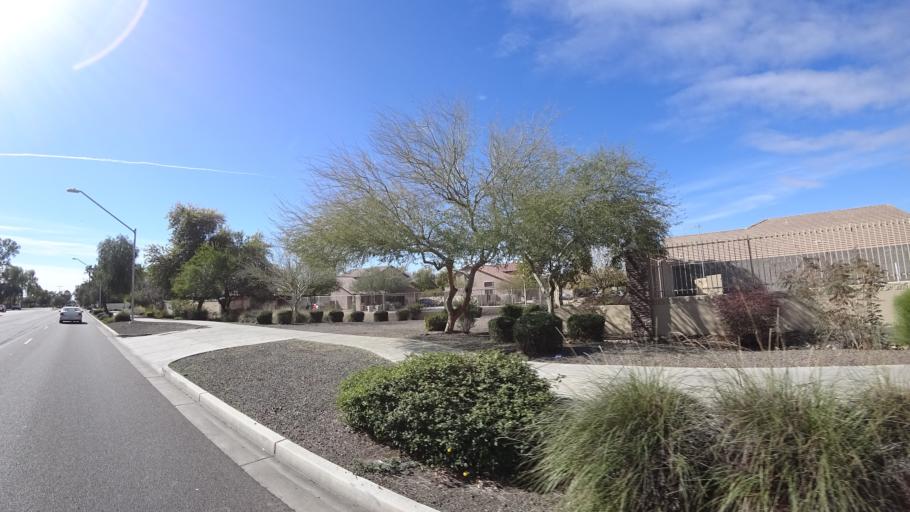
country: US
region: Arizona
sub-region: Maricopa County
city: Peoria
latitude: 33.5938
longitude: -112.1861
